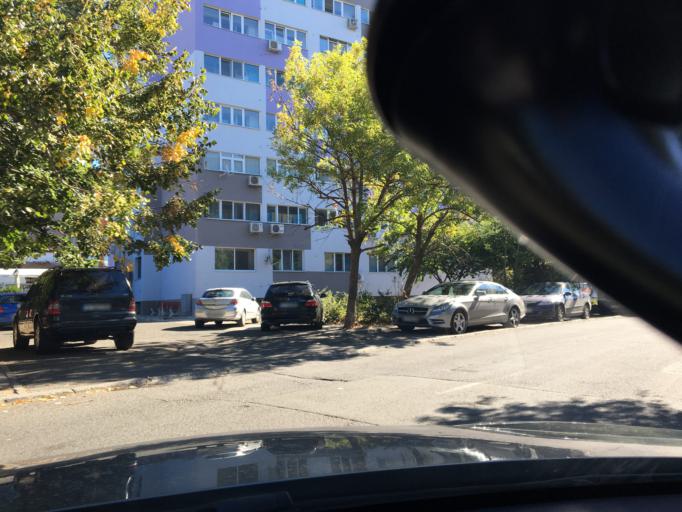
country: BG
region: Burgas
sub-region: Obshtina Burgas
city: Burgas
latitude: 42.5164
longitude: 27.4570
